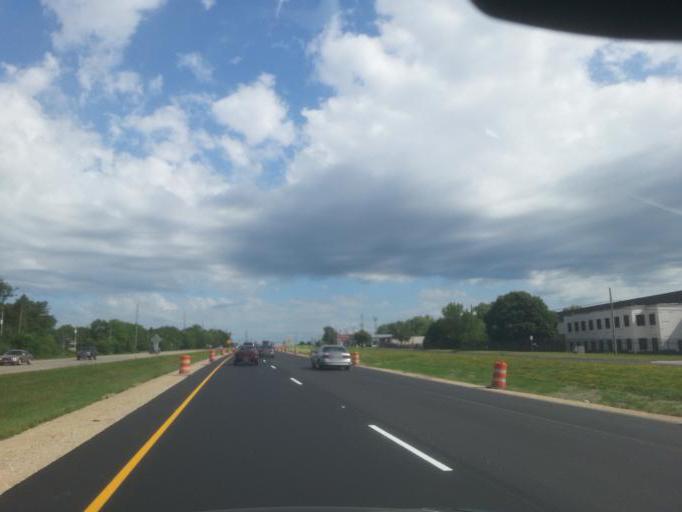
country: US
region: Wisconsin
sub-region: Dane County
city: Monona
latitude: 43.0566
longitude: -89.3092
